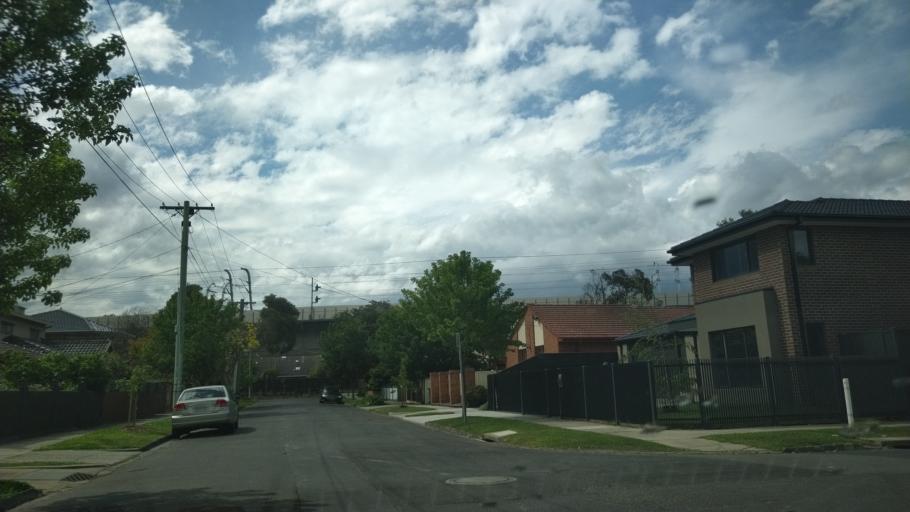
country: AU
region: Victoria
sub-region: Glen Eira
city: Carnegie
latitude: -37.8889
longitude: 145.0624
